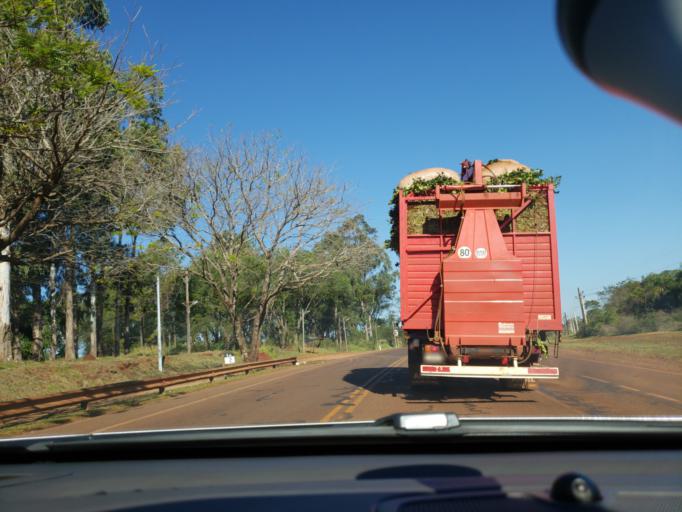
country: AR
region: Misiones
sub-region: Departamento de Apostoles
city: San Jose
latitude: -27.7625
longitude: -55.7718
